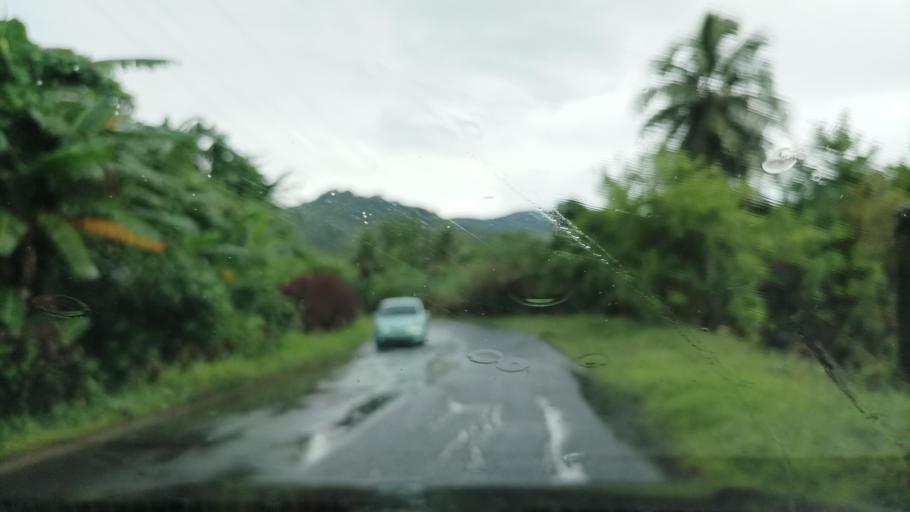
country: FM
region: Pohnpei
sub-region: Kolonia Municipality
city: Kolonia
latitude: 6.9526
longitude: 158.2303
